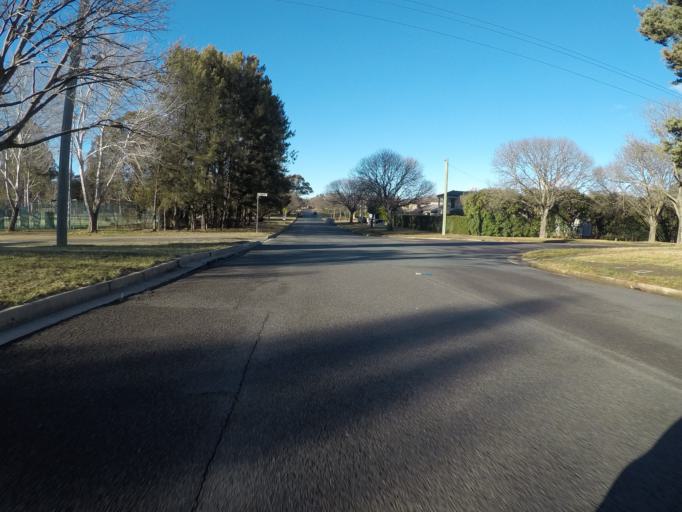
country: AU
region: Australian Capital Territory
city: Forrest
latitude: -35.3055
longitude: 149.0996
